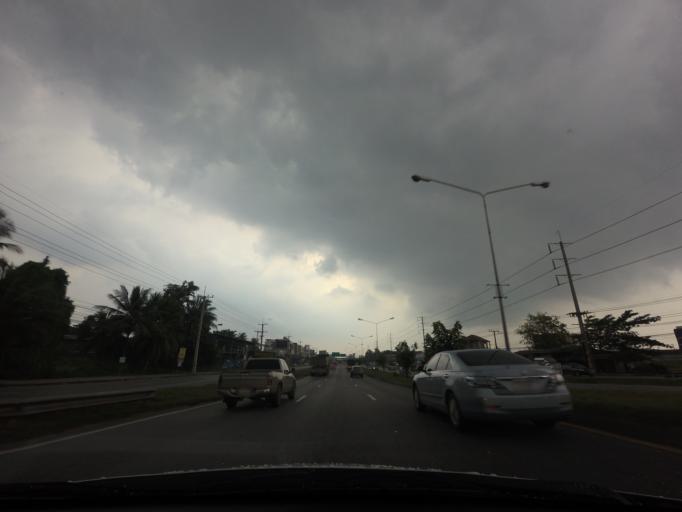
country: TH
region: Nakhon Pathom
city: Salaya
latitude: 13.7870
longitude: 100.3116
